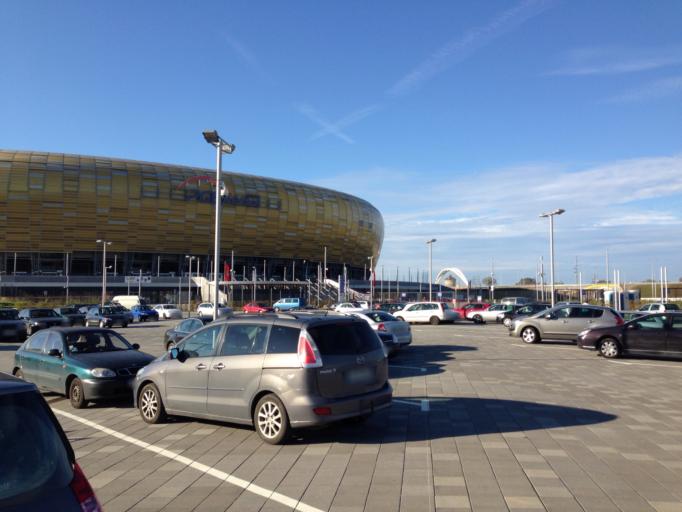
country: PL
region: Pomeranian Voivodeship
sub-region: Gdansk
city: Gdansk
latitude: 54.3887
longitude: 18.6443
